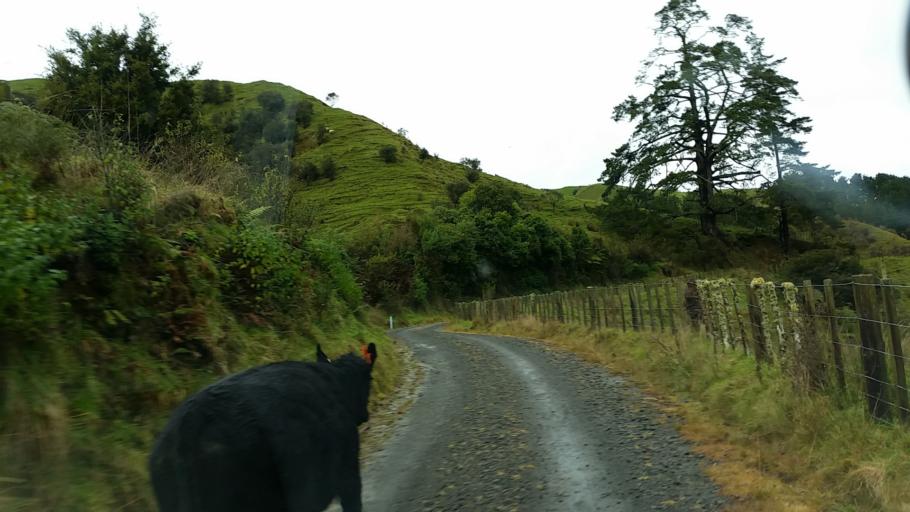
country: NZ
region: Taranaki
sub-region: South Taranaki District
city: Eltham
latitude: -39.4864
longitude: 174.4345
